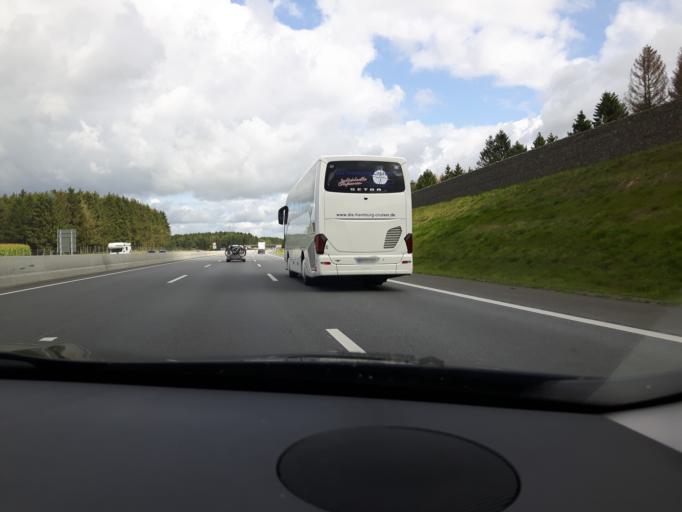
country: DE
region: Schleswig-Holstein
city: Kaltenkirchen
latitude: 53.8290
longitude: 9.9240
